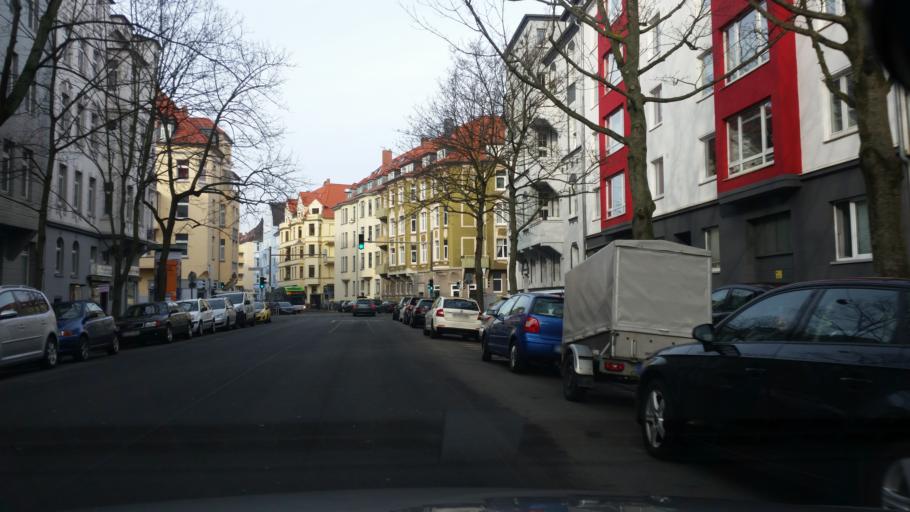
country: DE
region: Lower Saxony
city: Hannover
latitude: 52.3916
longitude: 9.7405
